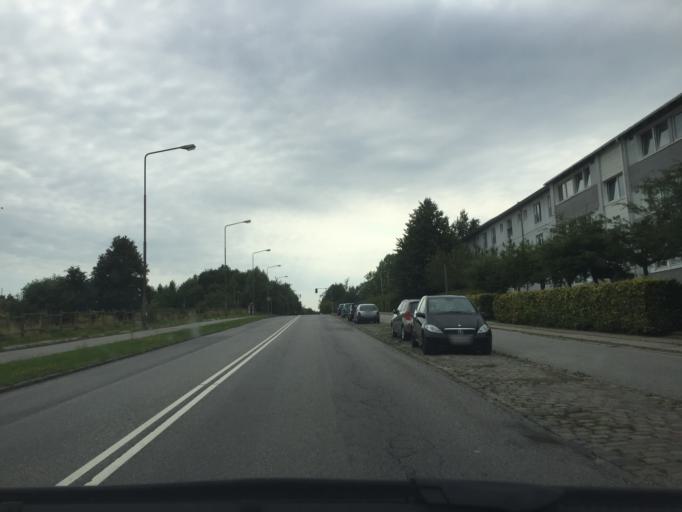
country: DK
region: Capital Region
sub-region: Lyngby-Tarbaek Kommune
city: Kongens Lyngby
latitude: 55.7967
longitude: 12.5298
